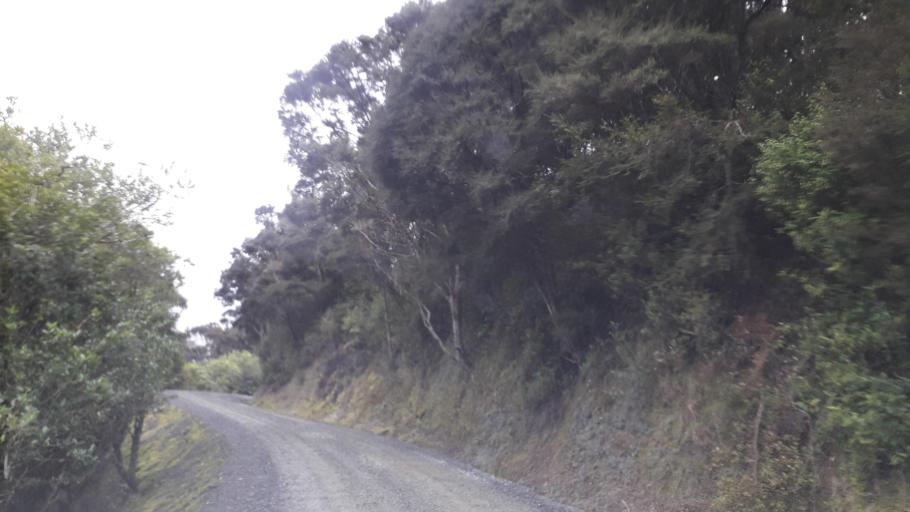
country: NZ
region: Northland
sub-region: Far North District
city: Waimate North
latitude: -35.1443
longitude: 173.7144
